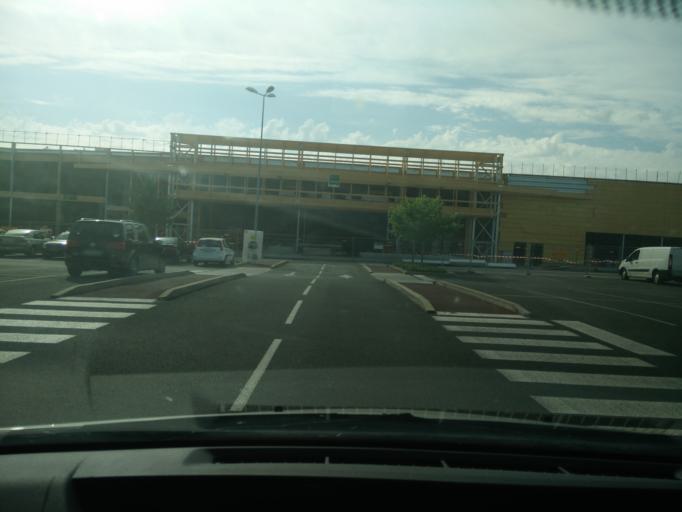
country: FR
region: Pays de la Loire
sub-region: Departement de Maine-et-Loire
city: Les Ponts-de-Ce
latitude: 47.4323
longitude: -0.4999
